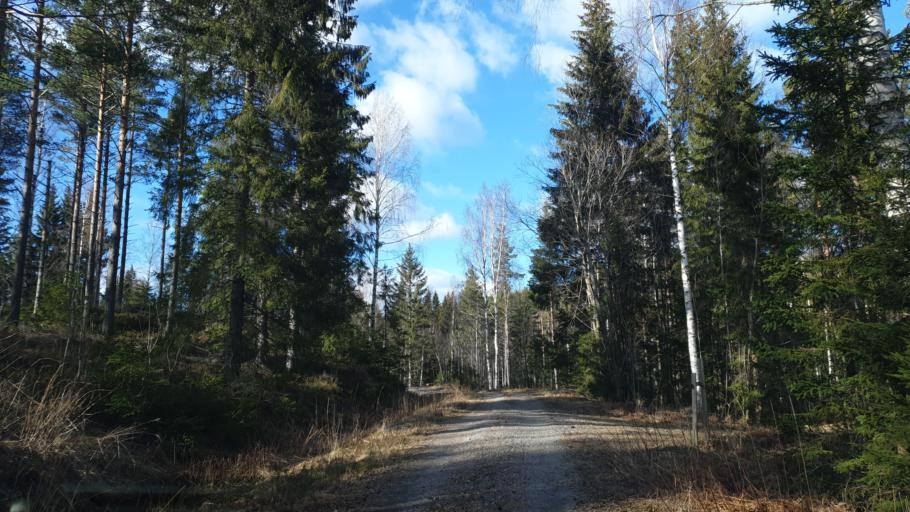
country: SE
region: OErebro
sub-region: Orebro Kommun
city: Garphyttan
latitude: 59.3758
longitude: 14.9757
